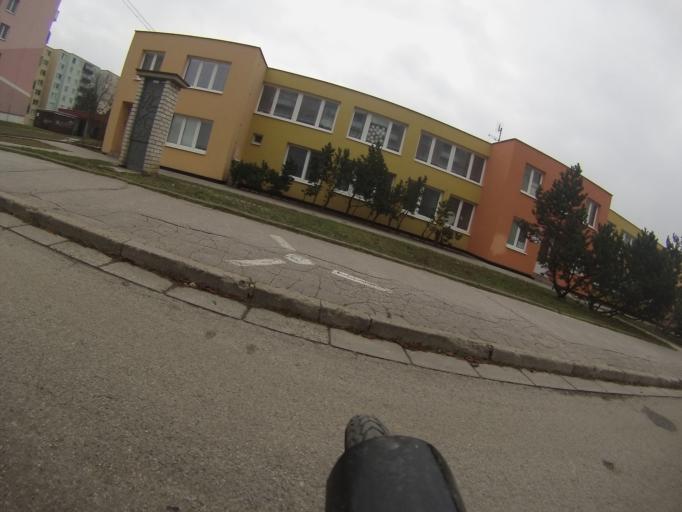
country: CZ
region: South Moravian
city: Bilovice nad Svitavou
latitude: 49.2111
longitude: 16.6858
